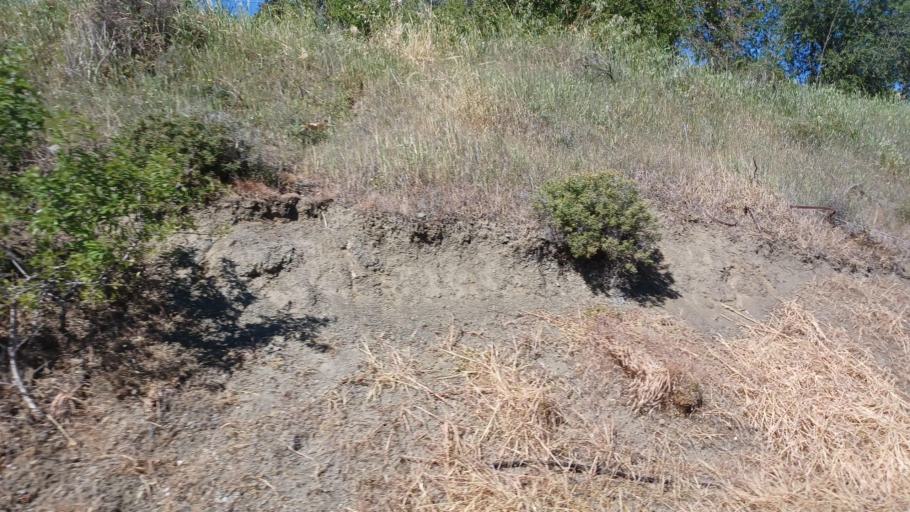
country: CY
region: Lefkosia
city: Peristerona
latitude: 35.0526
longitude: 33.0545
